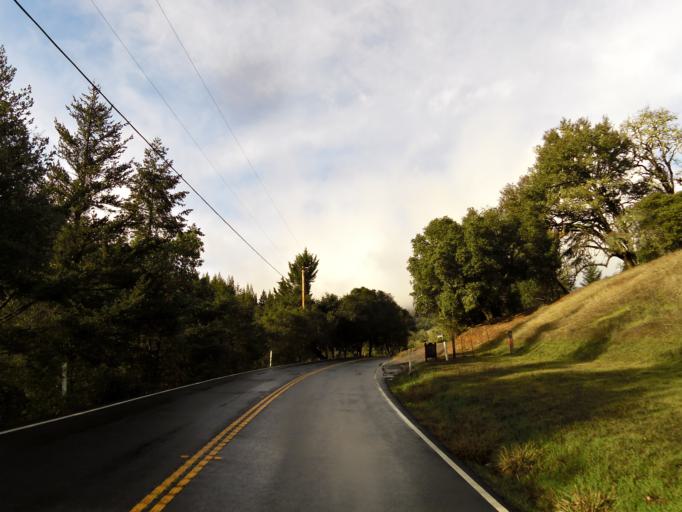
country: US
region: California
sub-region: Sonoma County
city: Cloverdale
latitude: 38.8810
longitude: -123.1152
